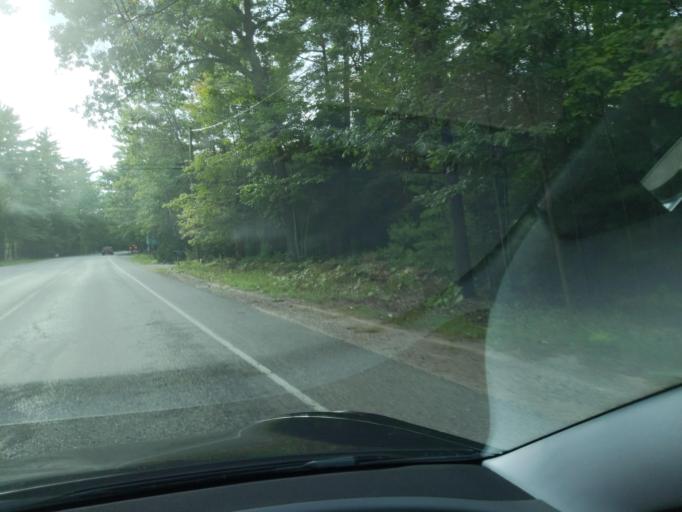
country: US
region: Michigan
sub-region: Kalkaska County
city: Rapid City
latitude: 44.8523
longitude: -85.3157
